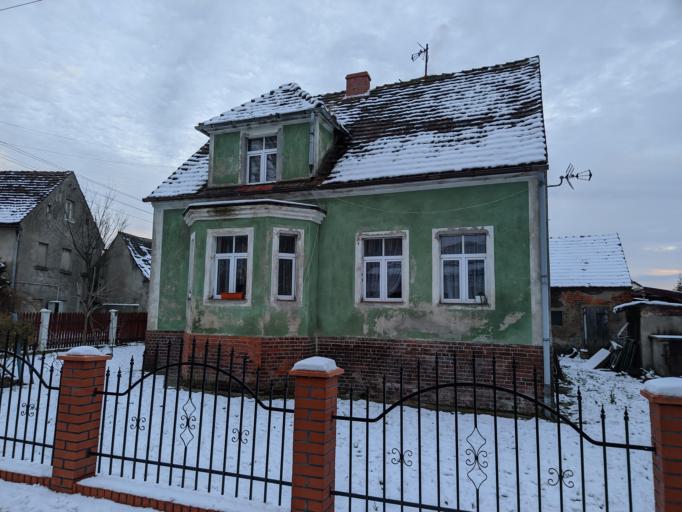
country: PL
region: Lower Silesian Voivodeship
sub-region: Powiat polkowicki
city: Przemkow
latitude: 51.5445
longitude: 15.7616
